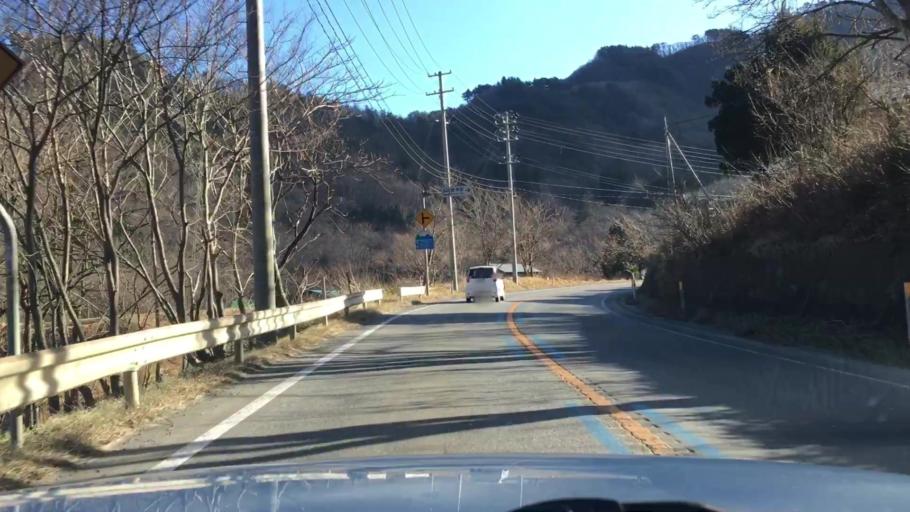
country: JP
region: Iwate
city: Miyako
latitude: 39.6048
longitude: 141.7727
